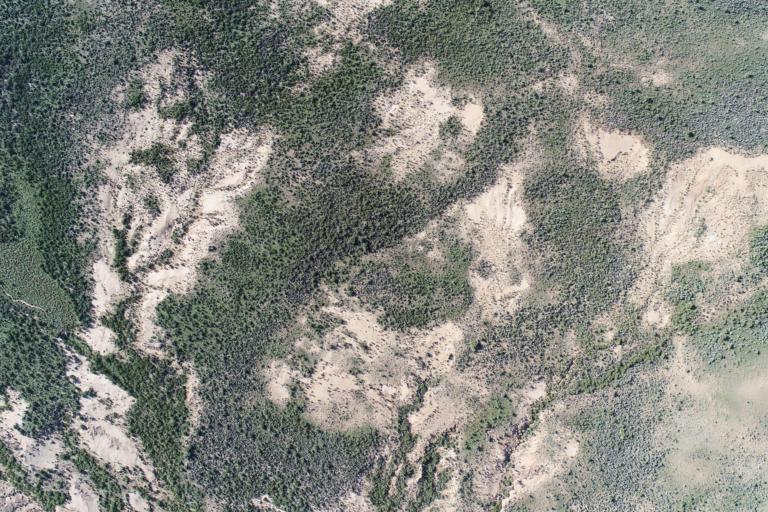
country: BO
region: La Paz
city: Curahuara de Carangas
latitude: -17.2997
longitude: -68.5099
